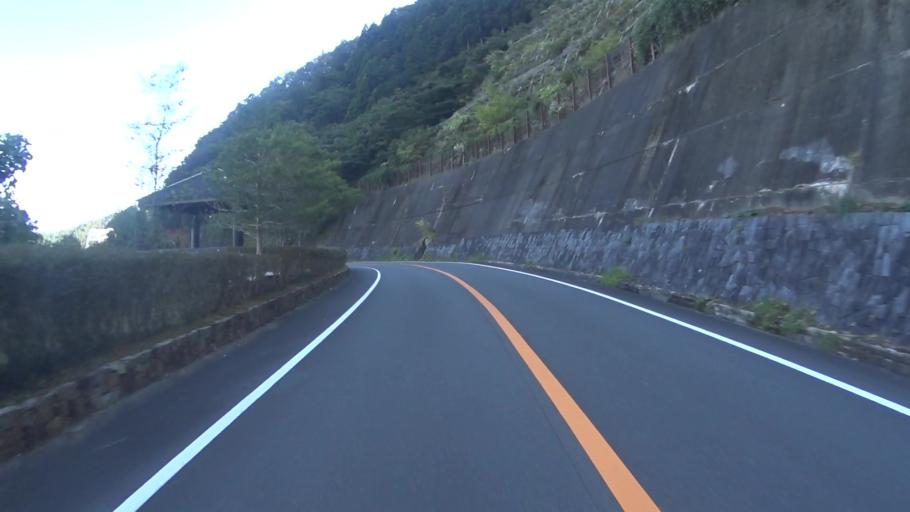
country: JP
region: Kyoto
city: Kameoka
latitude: 35.1476
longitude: 135.5153
